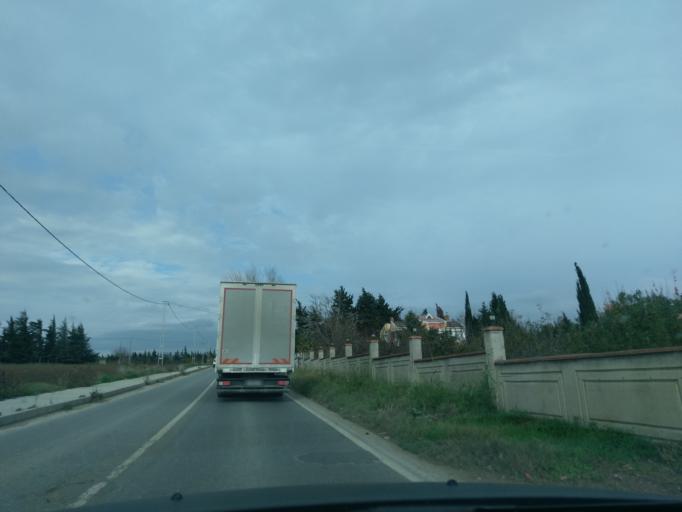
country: TR
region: Istanbul
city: Selimpasa
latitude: 41.0695
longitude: 28.3706
